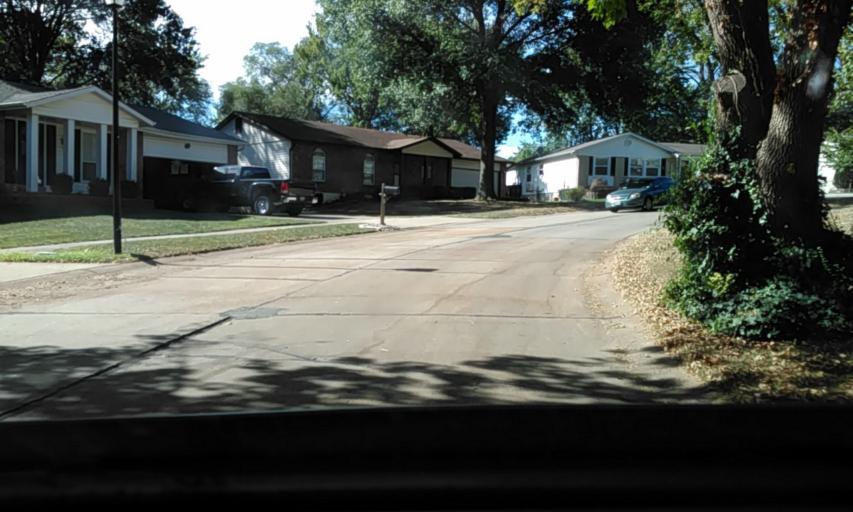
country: US
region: Missouri
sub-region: Jefferson County
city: Arnold
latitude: 38.4753
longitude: -90.3706
